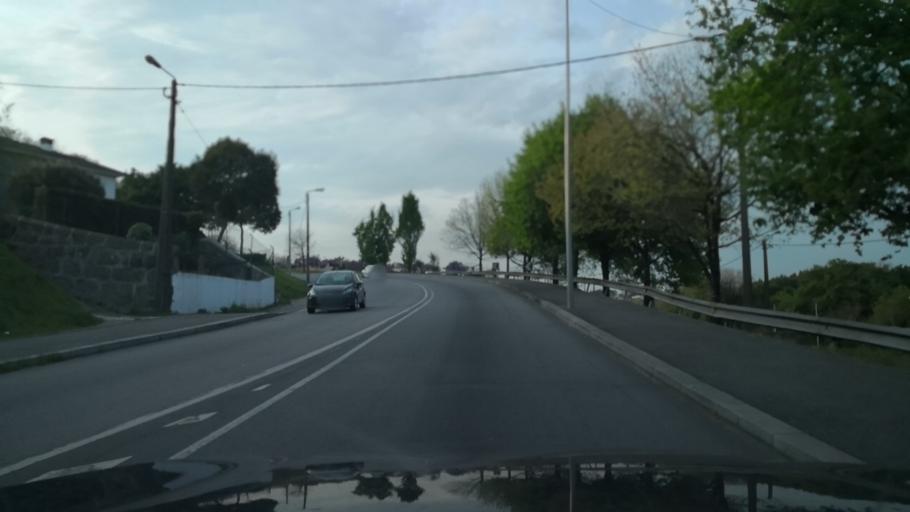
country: PT
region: Porto
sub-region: Maia
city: Leca do Bailio
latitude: 41.2065
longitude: -8.6210
